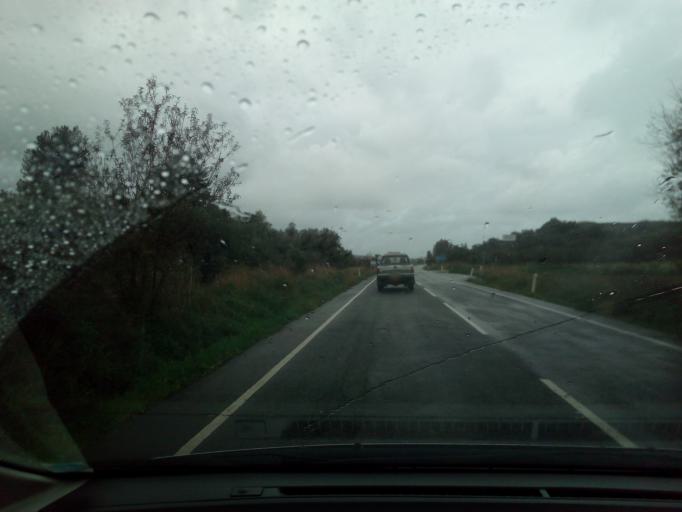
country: CY
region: Pafos
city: Polis
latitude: 35.0052
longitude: 32.4409
